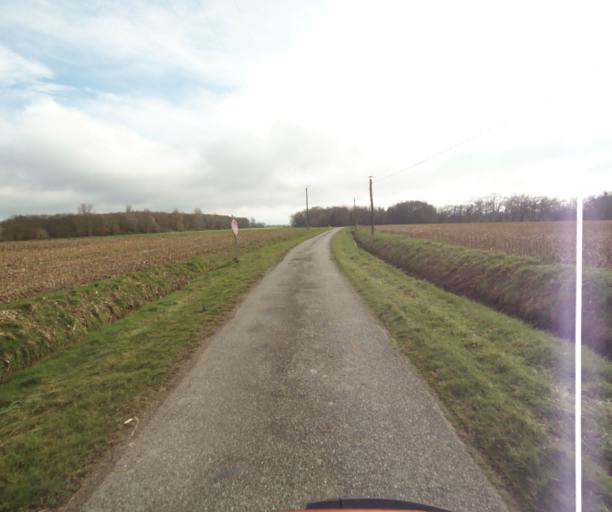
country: FR
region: Midi-Pyrenees
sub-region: Departement de l'Ariege
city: Mazeres
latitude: 43.2104
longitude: 1.6801
